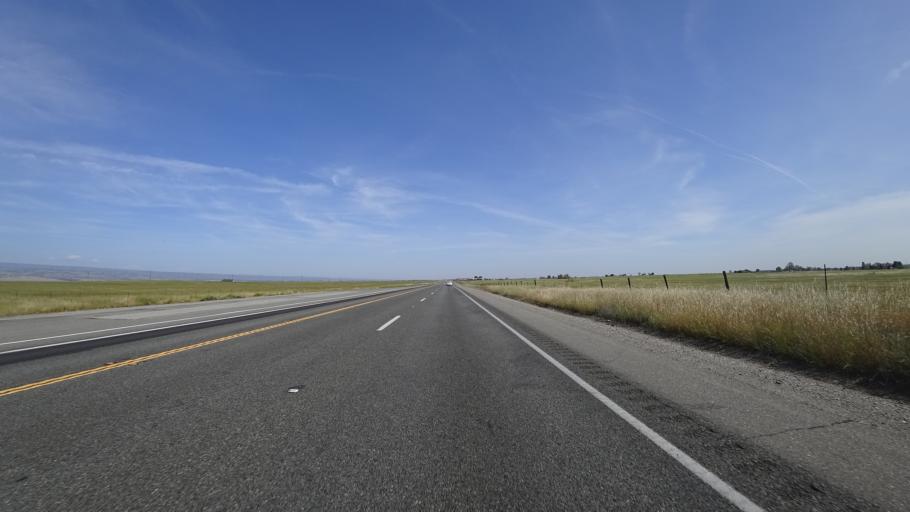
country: US
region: California
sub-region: Tehama County
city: Los Molinos
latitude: 39.9253
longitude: -122.0257
